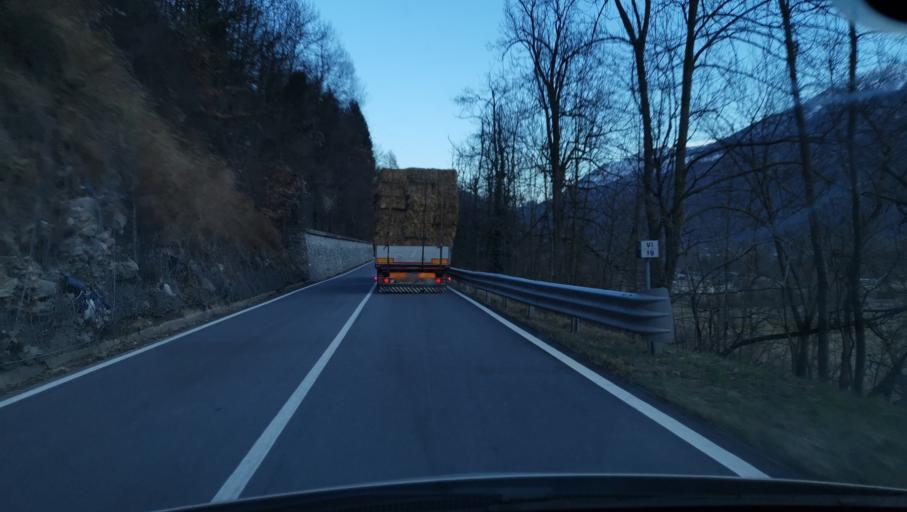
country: IT
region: Piedmont
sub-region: Provincia di Cuneo
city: Demonte
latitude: 44.3158
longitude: 7.2688
